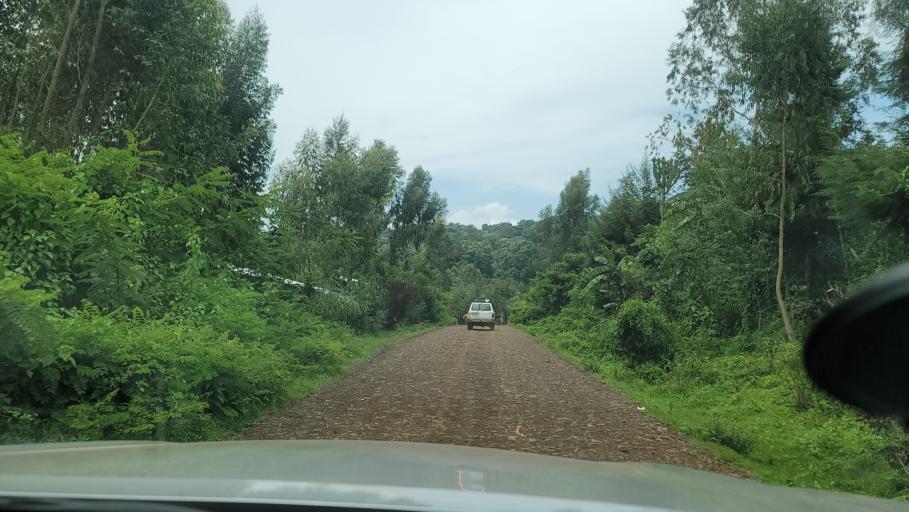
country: ET
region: Oromiya
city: Agaro
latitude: 7.7246
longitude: 36.2568
